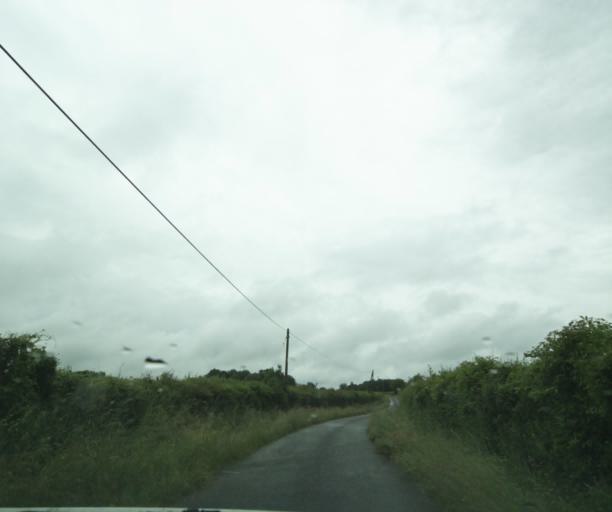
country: FR
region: Bourgogne
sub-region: Departement de Saone-et-Loire
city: Palinges
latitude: 46.5301
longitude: 4.2602
